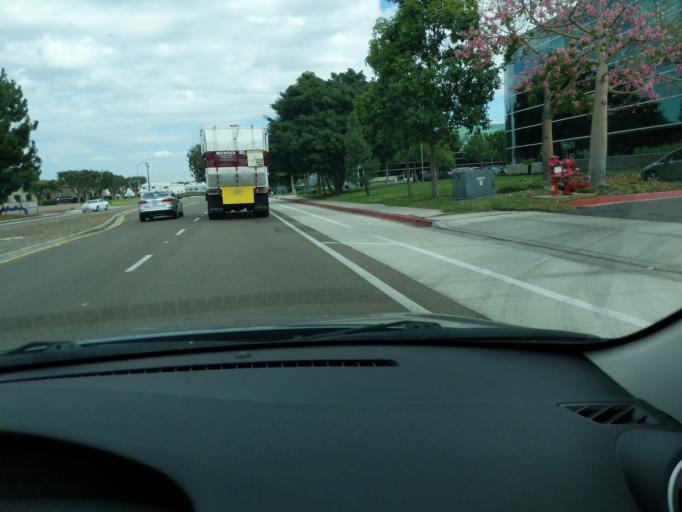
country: US
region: California
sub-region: San Diego County
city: San Diego
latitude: 32.8210
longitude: -117.1365
